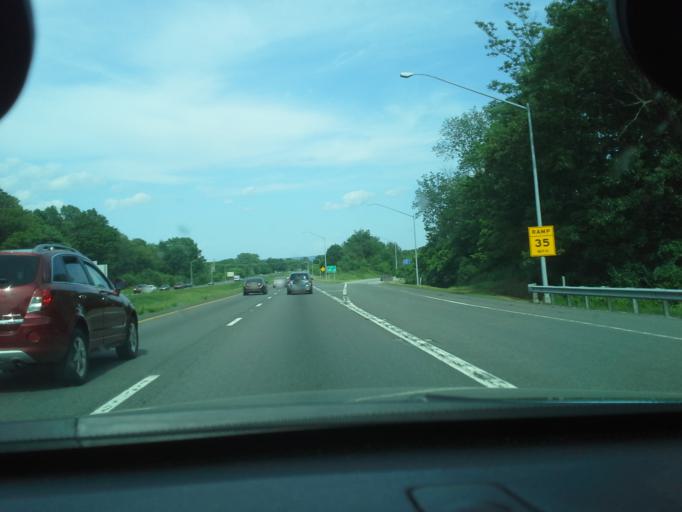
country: US
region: Maryland
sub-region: Washington County
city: Halfway
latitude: 39.6063
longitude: -77.7609
